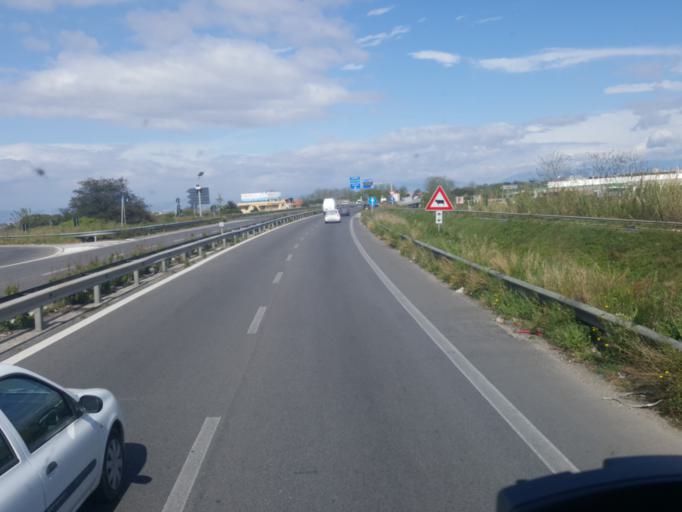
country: IT
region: Campania
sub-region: Provincia di Napoli
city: Qualiano
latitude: 40.9331
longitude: 14.1379
